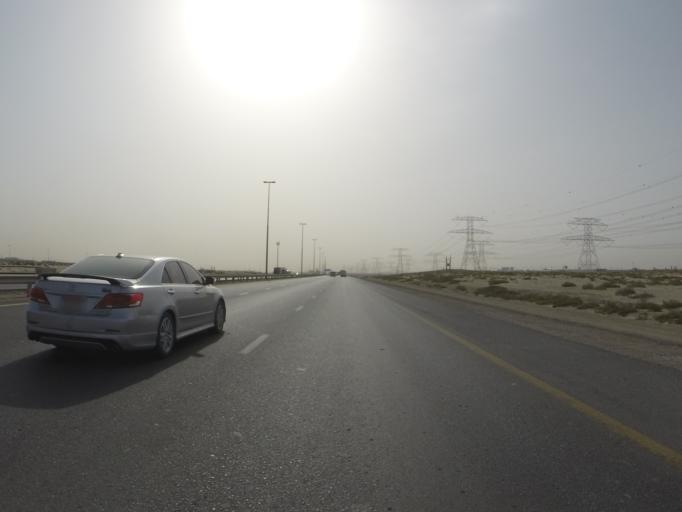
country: AE
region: Dubai
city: Dubai
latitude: 25.0170
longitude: 55.1223
